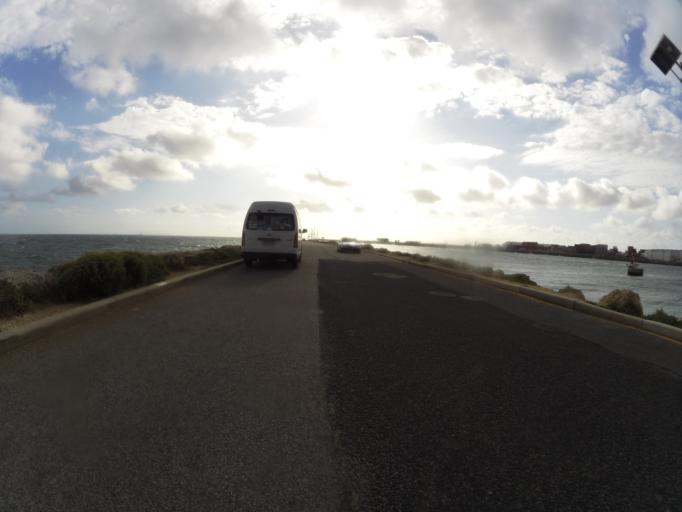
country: AU
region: Western Australia
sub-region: Fremantle
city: South Fremantle
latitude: -32.0560
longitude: 115.7367
